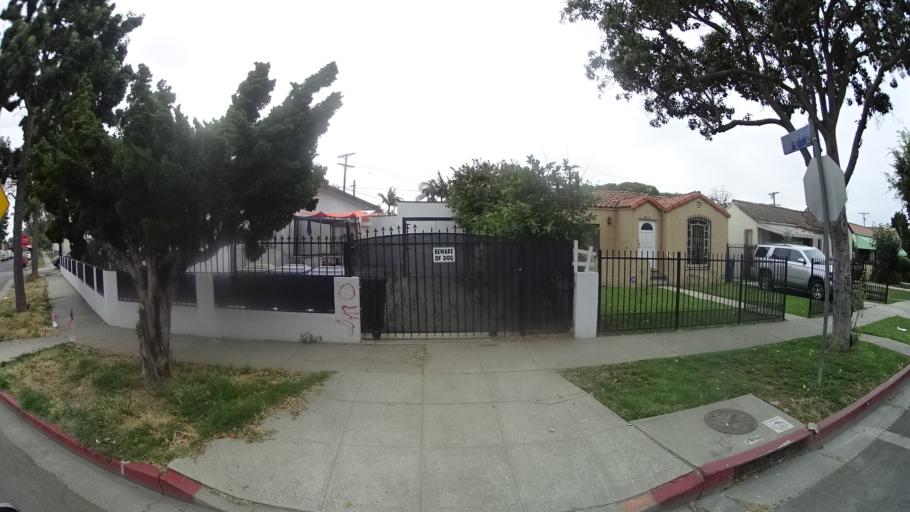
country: US
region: California
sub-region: Los Angeles County
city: View Park-Windsor Hills
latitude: 34.0276
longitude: -118.3471
